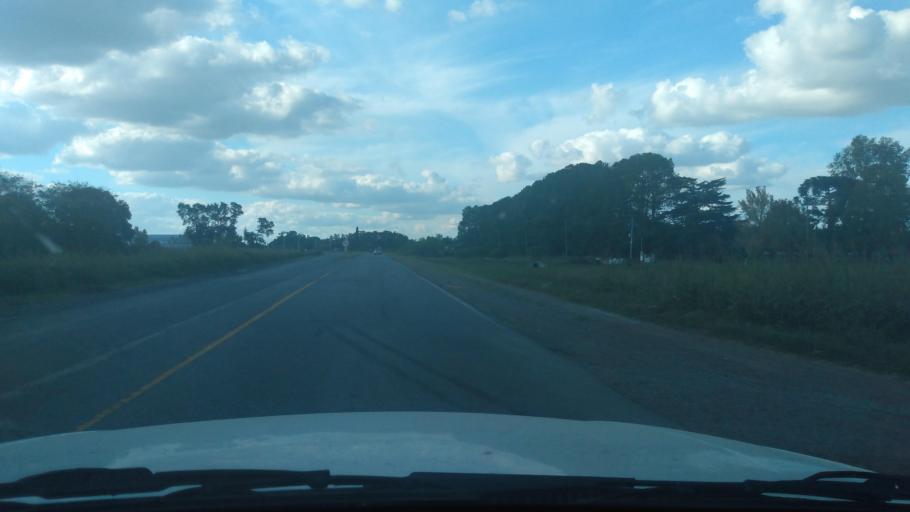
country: AR
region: Buenos Aires
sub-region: Partido de Mercedes
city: Mercedes
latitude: -34.6737
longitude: -59.4003
